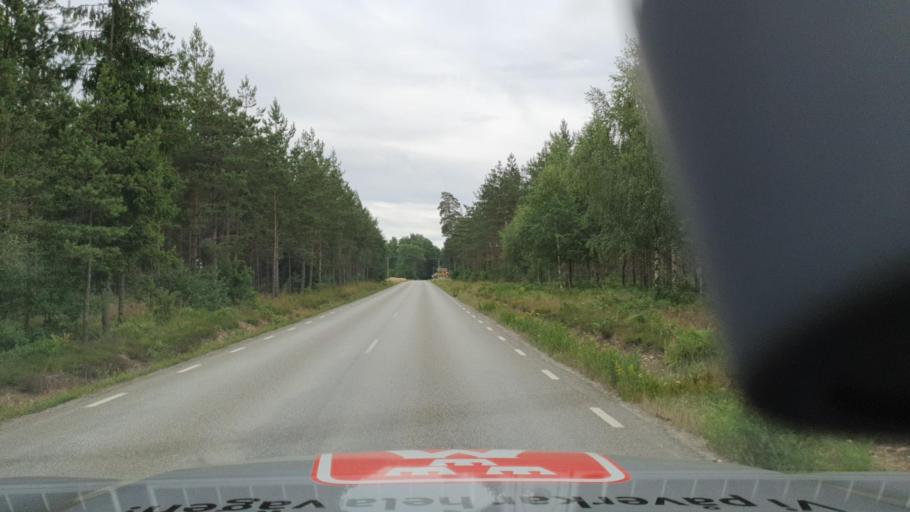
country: SE
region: Kalmar
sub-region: Kalmar Kommun
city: Trekanten
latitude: 56.6391
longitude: 16.0267
